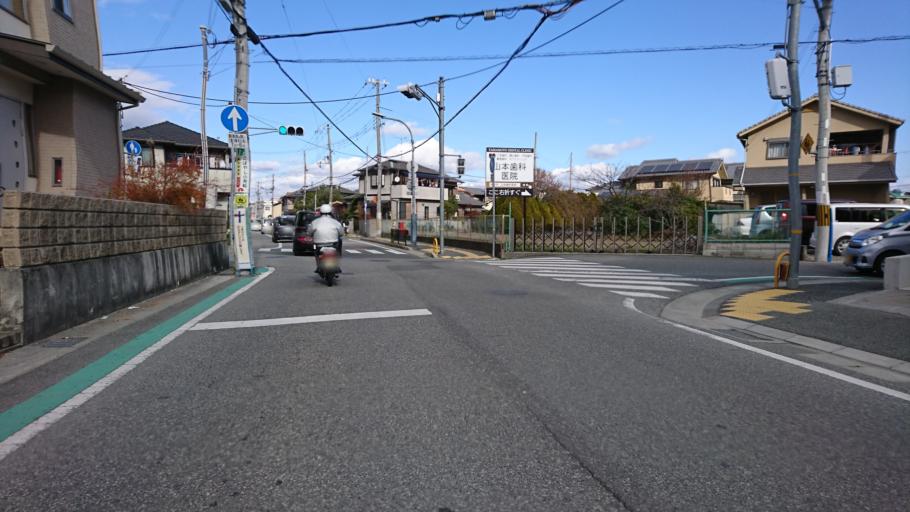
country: JP
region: Hyogo
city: Kakogawacho-honmachi
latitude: 34.7823
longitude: 134.8038
